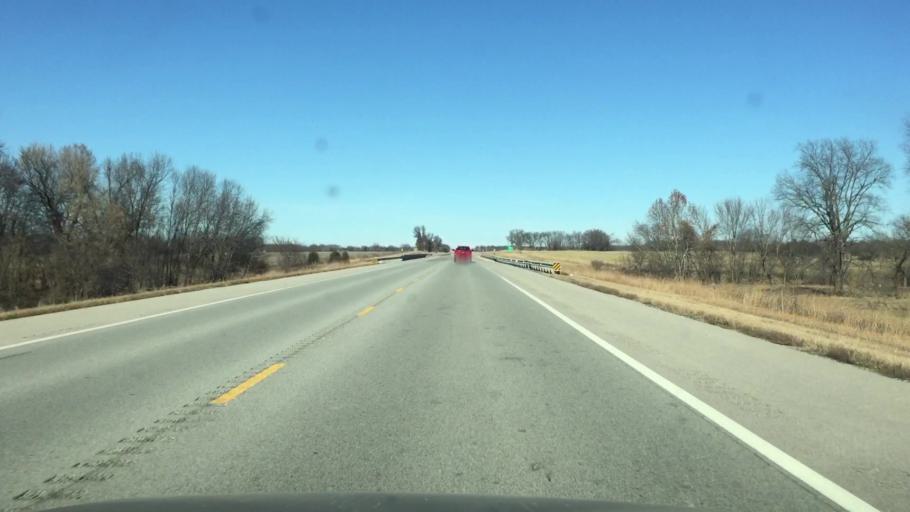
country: US
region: Kansas
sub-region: Allen County
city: Iola
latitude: 37.9848
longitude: -95.3810
